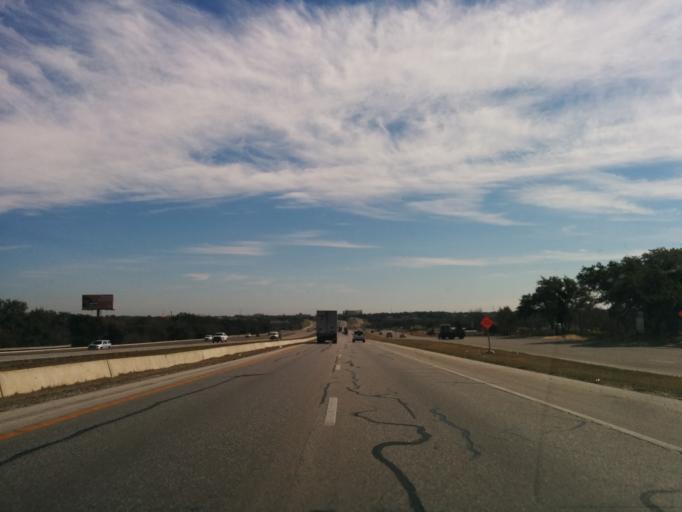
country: US
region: Texas
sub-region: Bexar County
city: Shavano Park
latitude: 29.6014
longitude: -98.5505
